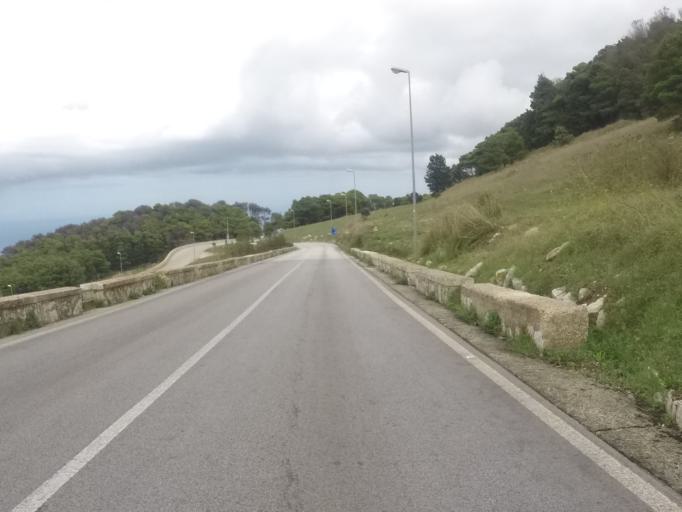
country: IT
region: Sicily
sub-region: Trapani
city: Erice
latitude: 38.0413
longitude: 12.5829
